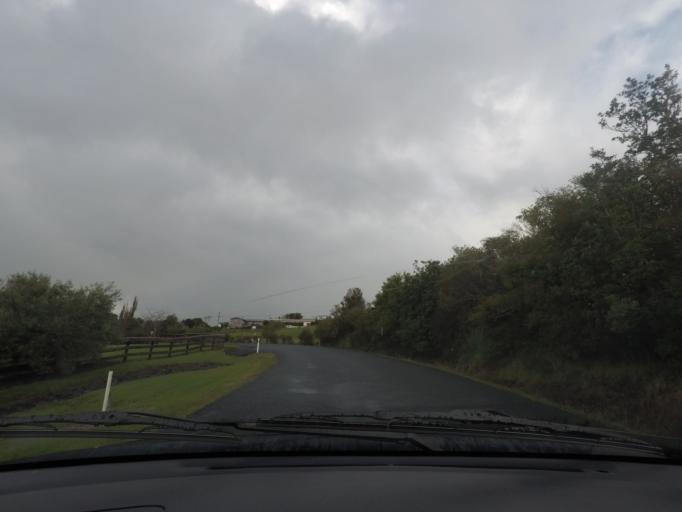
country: NZ
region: Auckland
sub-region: Auckland
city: Warkworth
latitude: -36.4290
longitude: 174.7316
